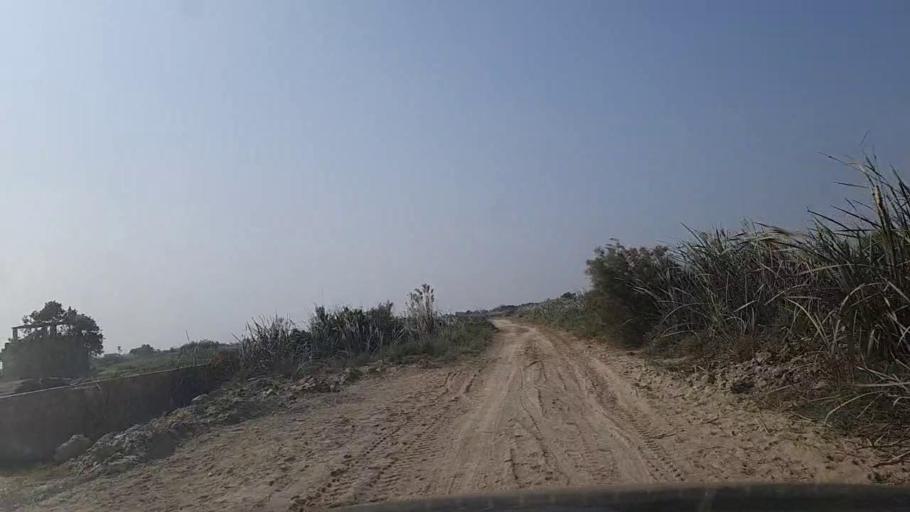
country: PK
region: Sindh
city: Gharo
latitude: 24.7140
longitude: 67.6559
